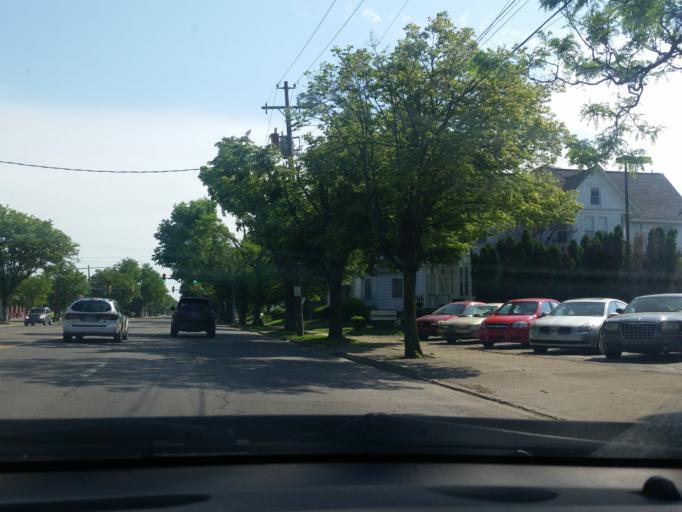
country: US
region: Pennsylvania
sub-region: Luzerne County
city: Kingston
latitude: 41.2642
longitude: -75.8945
